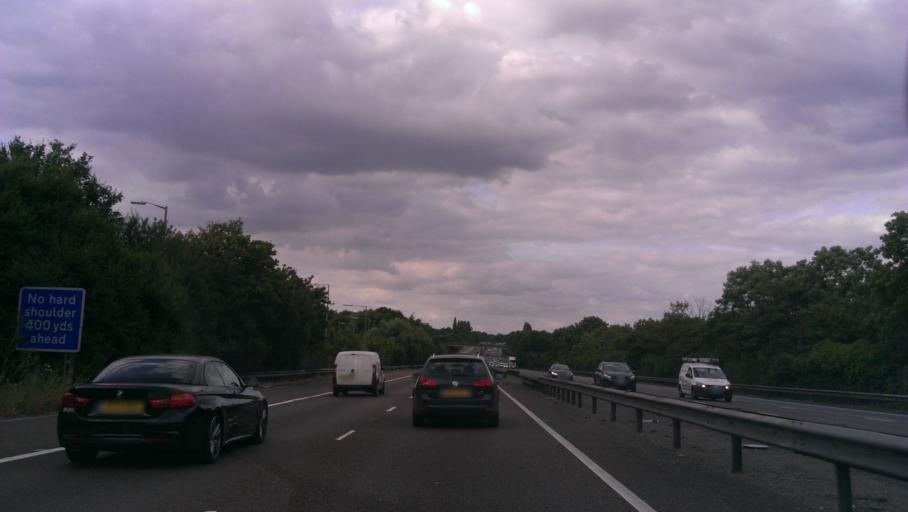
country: GB
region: England
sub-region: Essex
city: Ingatestone
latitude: 51.6589
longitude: 0.3646
